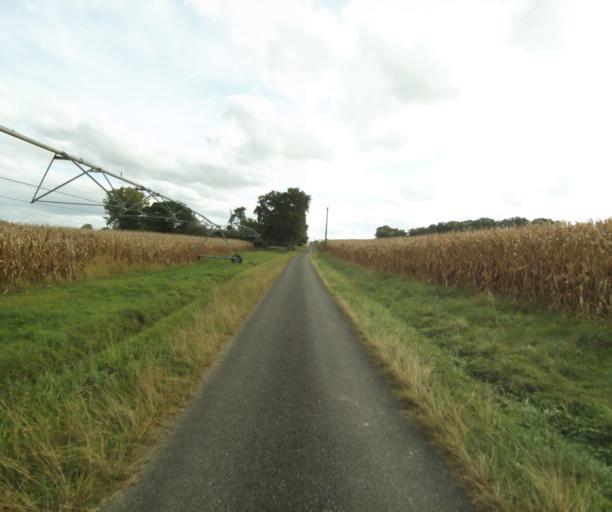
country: FR
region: Midi-Pyrenees
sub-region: Departement du Gers
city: Gondrin
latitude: 43.8561
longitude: 0.2229
